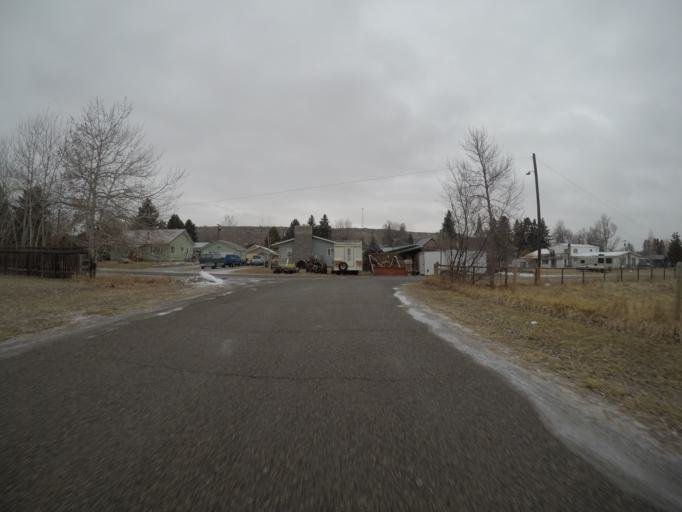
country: US
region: Montana
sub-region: Stillwater County
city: Absarokee
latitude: 45.5147
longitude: -109.4442
